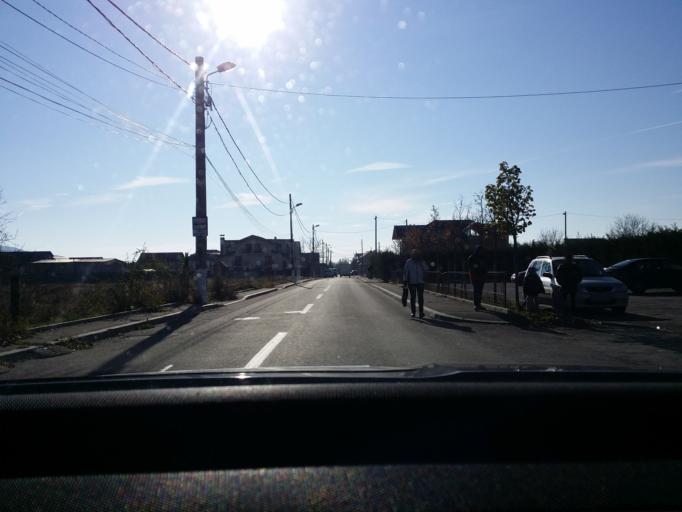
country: RO
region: Prahova
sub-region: Municipiul Campina
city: Campina
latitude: 45.1432
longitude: 25.7274
